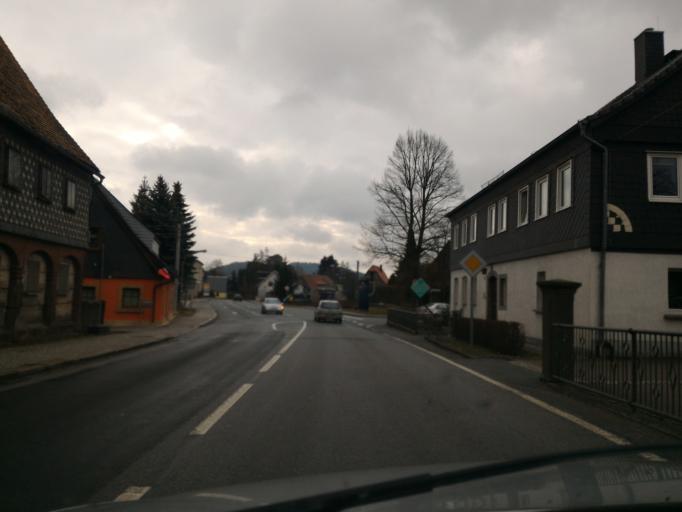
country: DE
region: Saxony
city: Eibau
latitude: 50.9795
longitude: 14.6661
